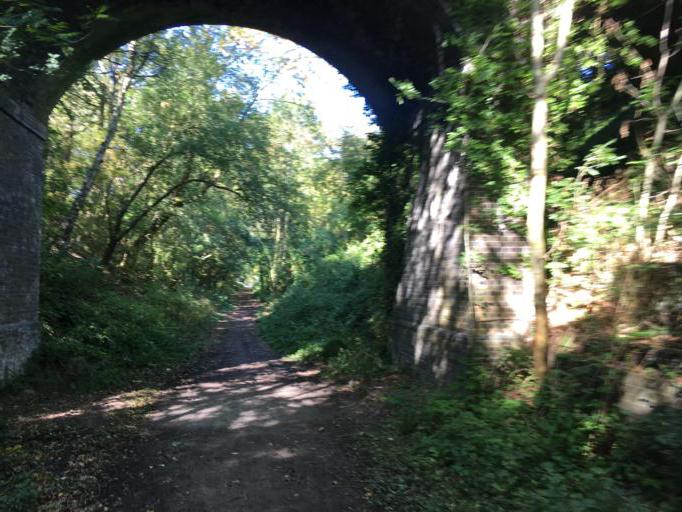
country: GB
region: England
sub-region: Warwickshire
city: Kenilworth
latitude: 52.3813
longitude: -1.6079
